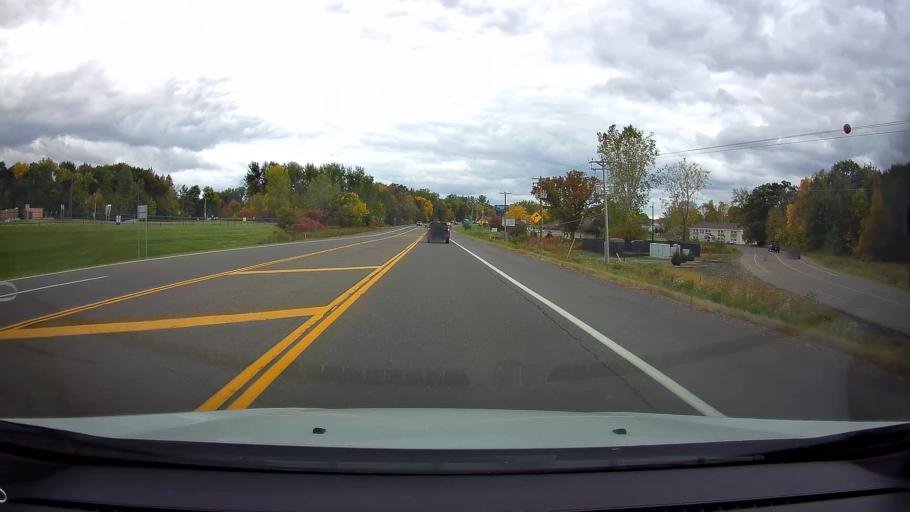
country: US
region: Minnesota
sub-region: Chisago County
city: Lindstrom
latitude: 45.3832
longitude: -92.8695
